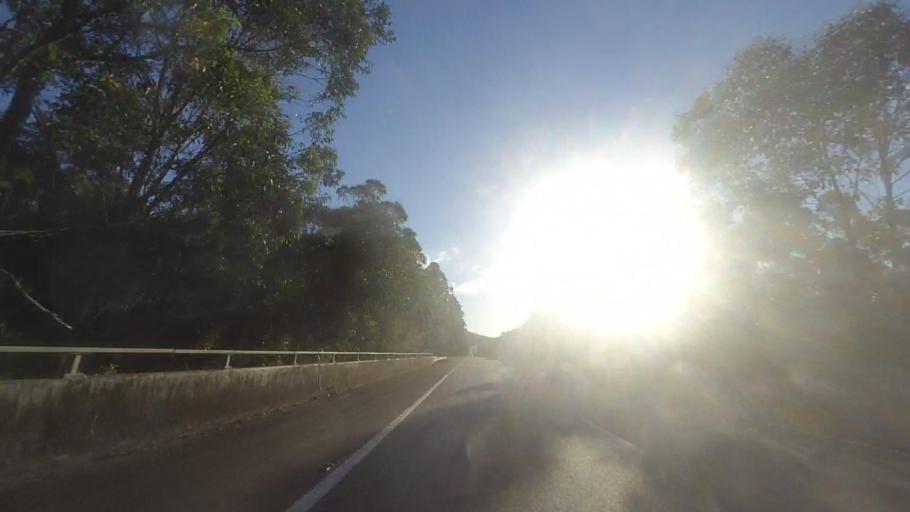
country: AU
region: New South Wales
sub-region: Great Lakes
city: Bulahdelah
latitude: -32.3767
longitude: 152.2751
